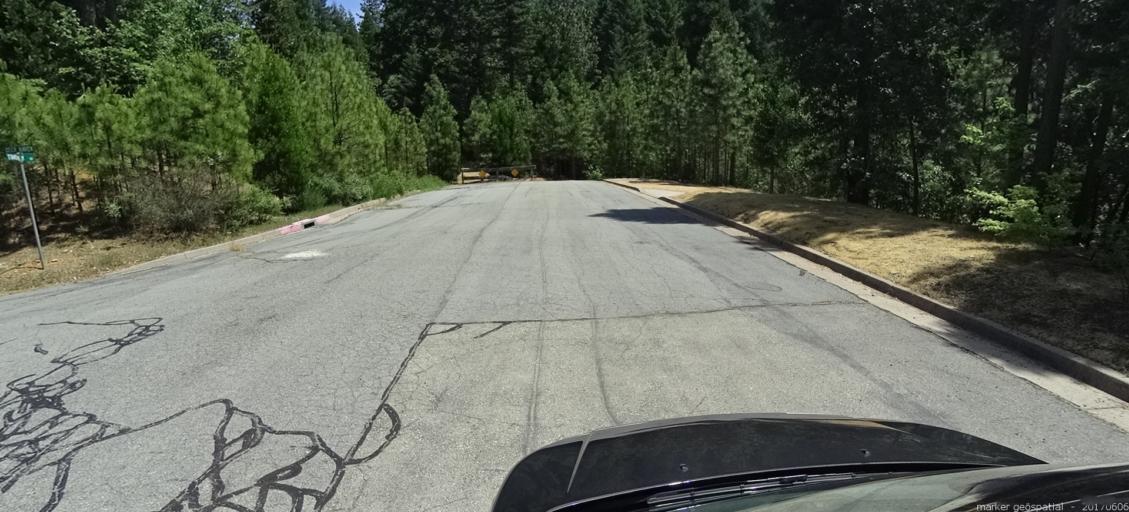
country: US
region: California
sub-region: Siskiyou County
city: Dunsmuir
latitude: 41.2288
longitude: -122.2709
